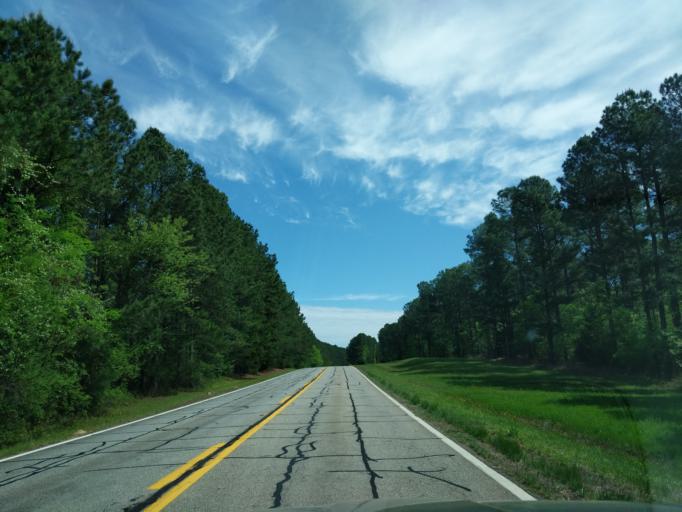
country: US
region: Georgia
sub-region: Columbia County
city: Appling
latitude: 33.6171
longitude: -82.2941
